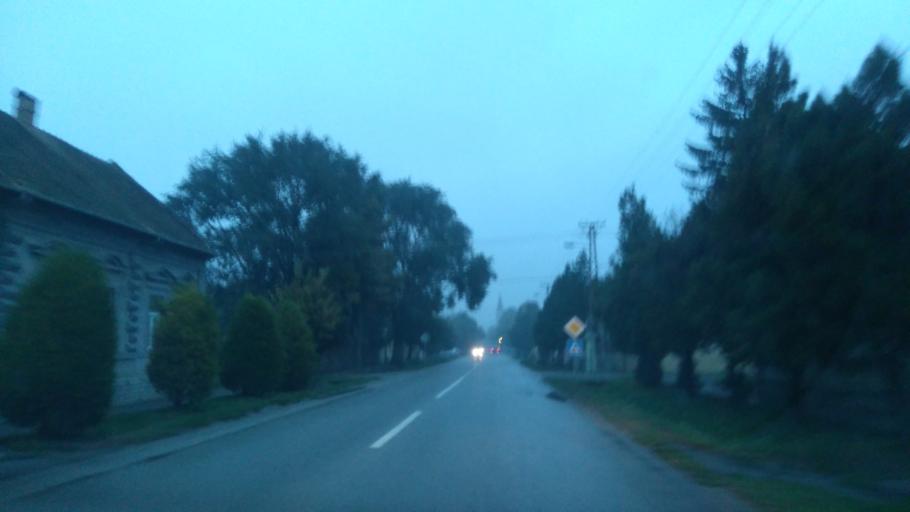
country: RS
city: Backo Petrovo Selo
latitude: 45.7008
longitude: 20.0856
